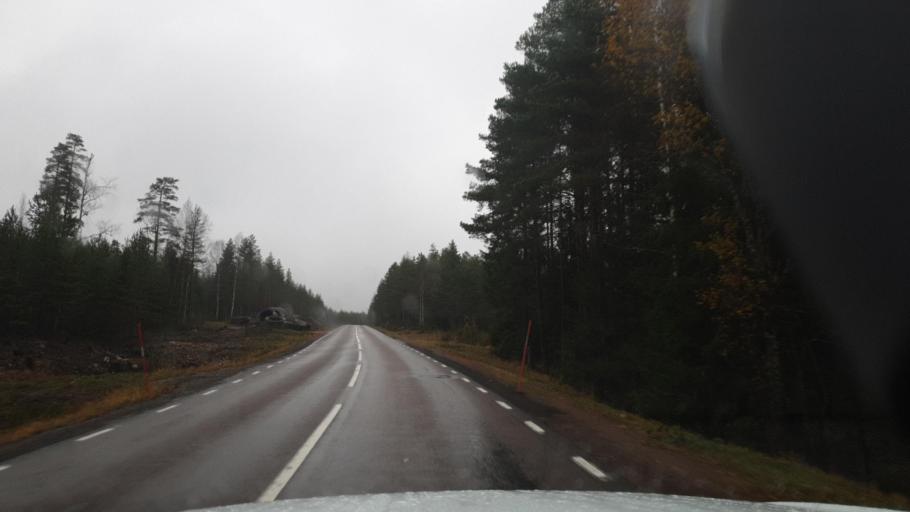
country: SE
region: Vaermland
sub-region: Sunne Kommun
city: Sunne
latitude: 59.6832
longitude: 13.0476
